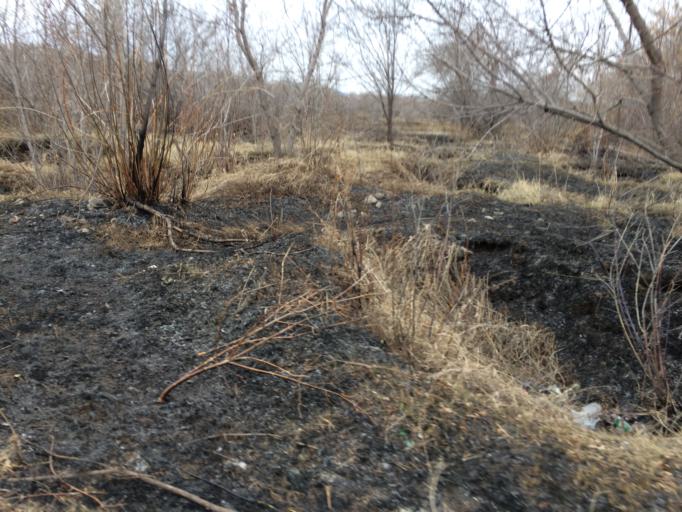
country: RU
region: Chelyabinsk
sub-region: Gorod Magnitogorsk
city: Magnitogorsk
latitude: 53.4404
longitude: 58.9768
